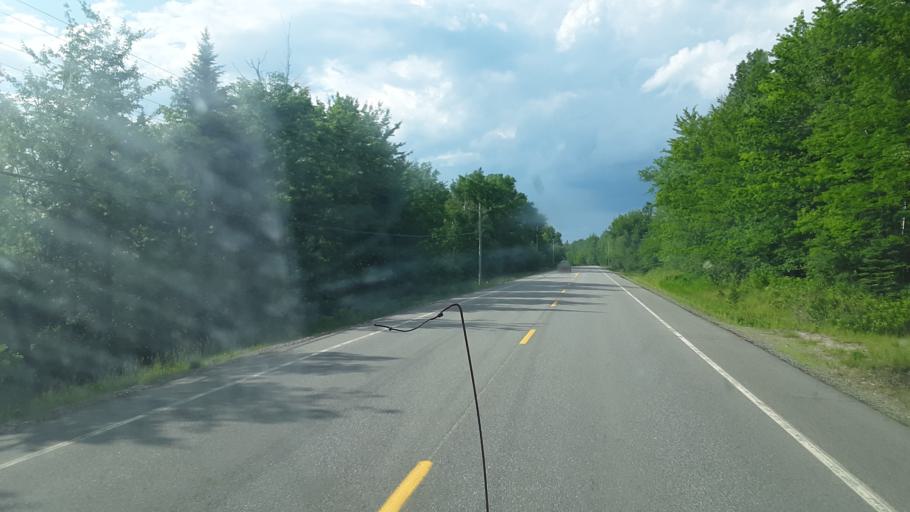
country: US
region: Maine
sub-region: Washington County
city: Machias
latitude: 45.0089
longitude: -67.5540
